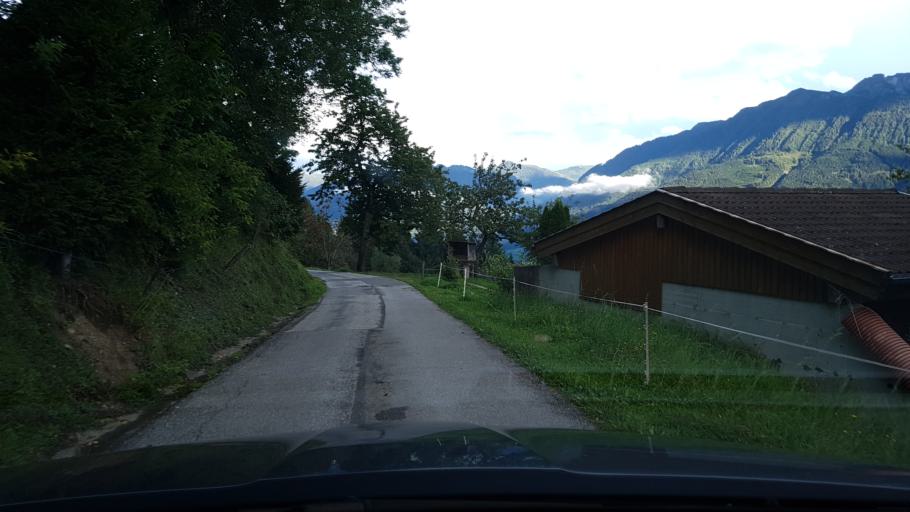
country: AT
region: Salzburg
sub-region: Politischer Bezirk Sankt Johann im Pongau
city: Goldegg
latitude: 47.3391
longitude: 13.0983
